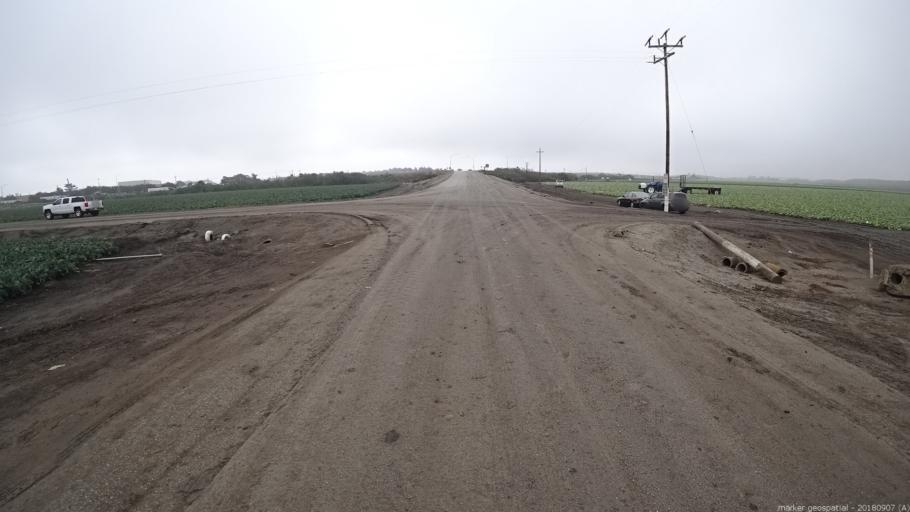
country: US
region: California
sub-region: Monterey County
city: Marina
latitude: 36.7284
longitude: -121.7910
